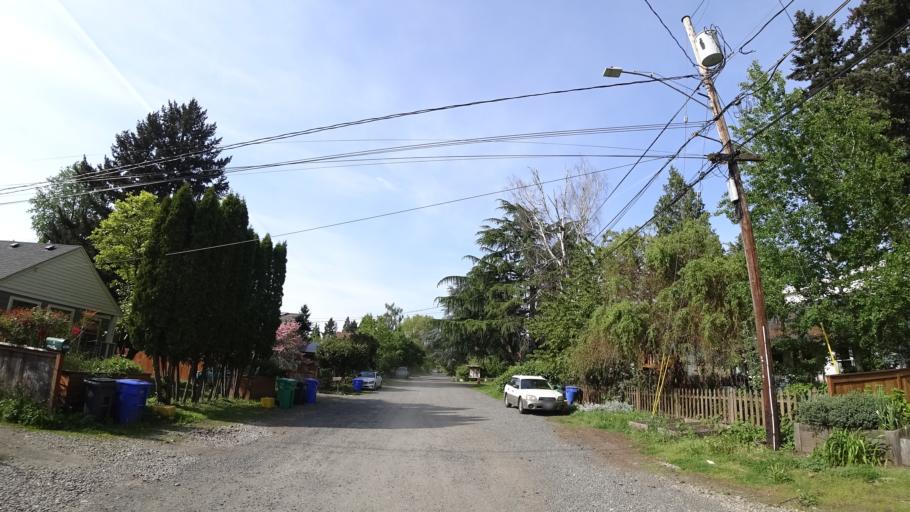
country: US
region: Oregon
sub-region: Clackamas County
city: Milwaukie
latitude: 45.4754
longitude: -122.6114
